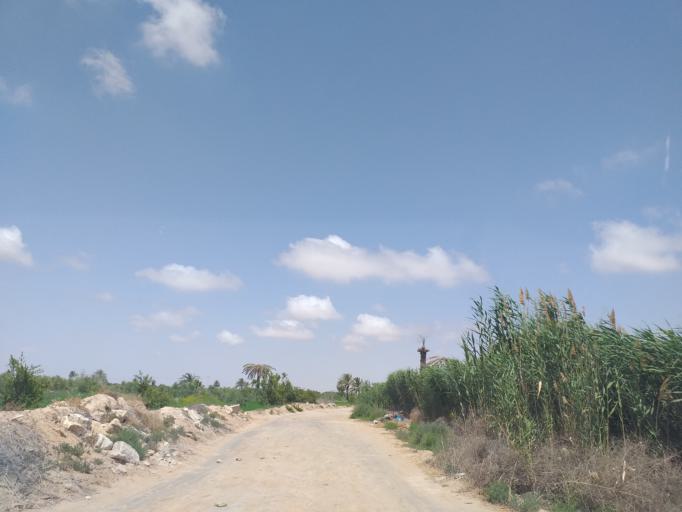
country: TN
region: Qabis
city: Gabes
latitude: 33.9519
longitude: 10.0487
